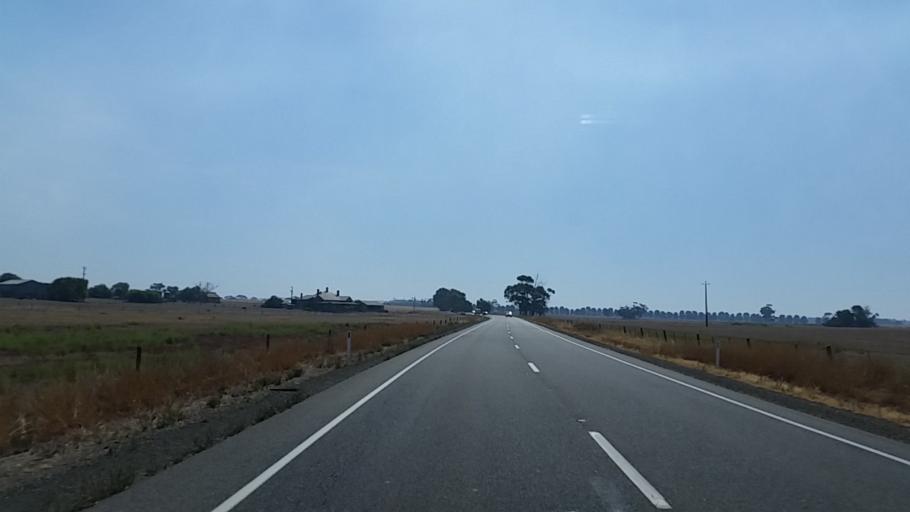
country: AU
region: South Australia
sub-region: Light
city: Kapunda
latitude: -34.2477
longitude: 138.7487
